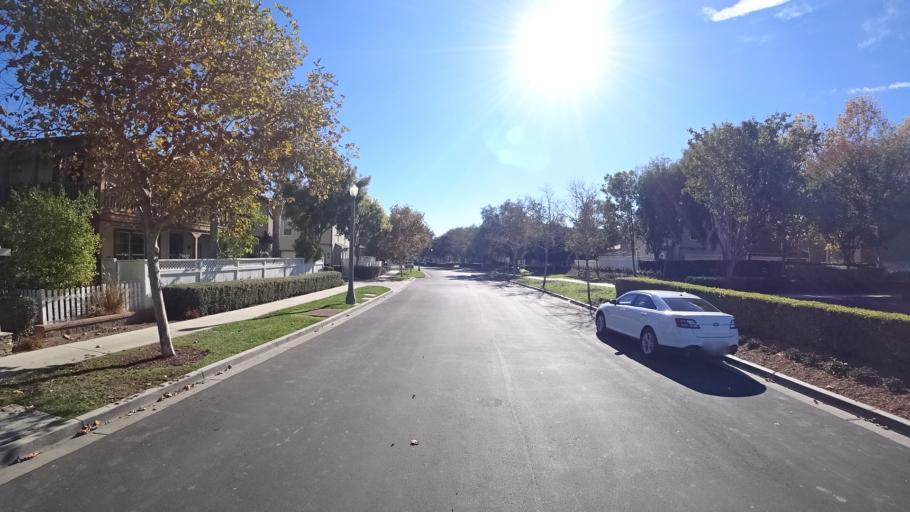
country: US
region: California
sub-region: Orange County
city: Ladera Ranch
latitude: 33.5501
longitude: -117.6438
